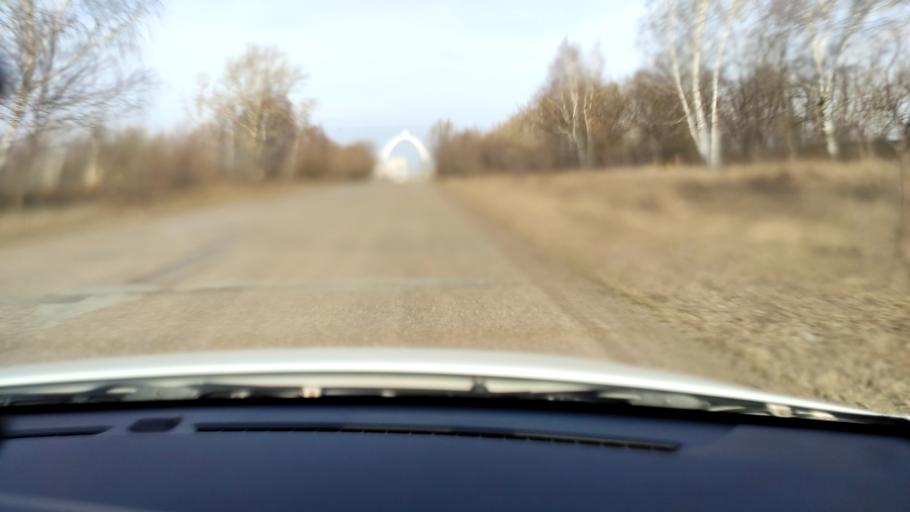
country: RU
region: Tatarstan
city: Stolbishchi
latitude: 55.7227
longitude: 49.2058
